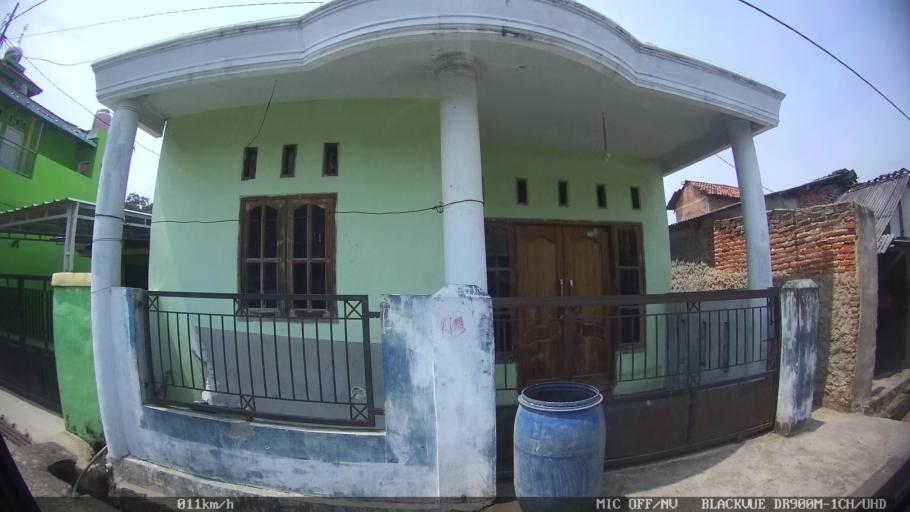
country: ID
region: Lampung
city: Bandarlampung
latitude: -5.4600
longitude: 105.2501
